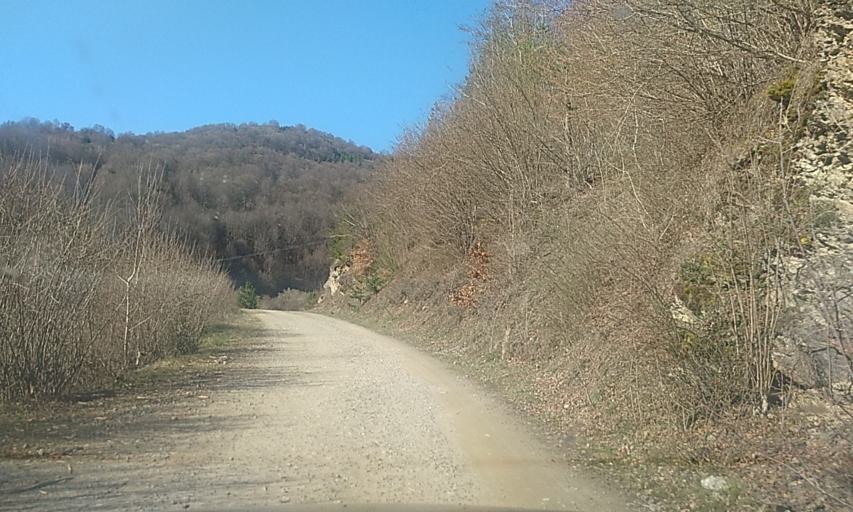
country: MK
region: Kriva Palanka
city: Kriva Palanka
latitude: 42.3422
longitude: 22.3924
